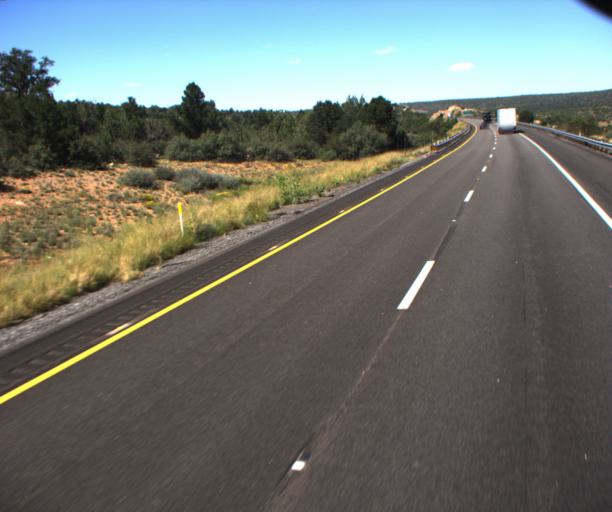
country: US
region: Arizona
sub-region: Mohave County
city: Peach Springs
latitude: 35.2096
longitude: -113.2853
